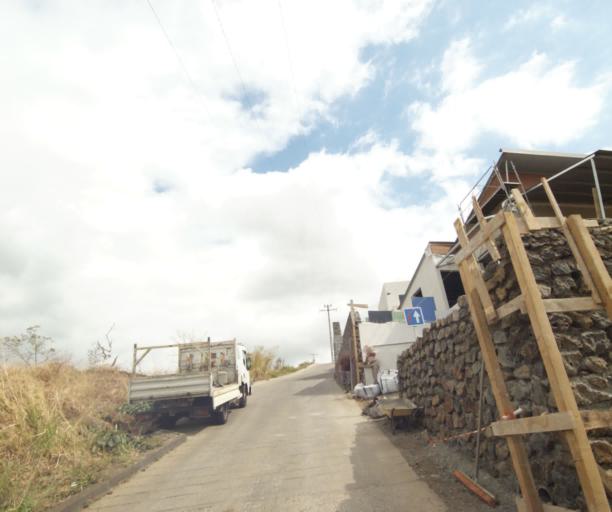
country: RE
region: Reunion
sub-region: Reunion
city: Saint-Paul
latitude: -21.0241
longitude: 55.2933
